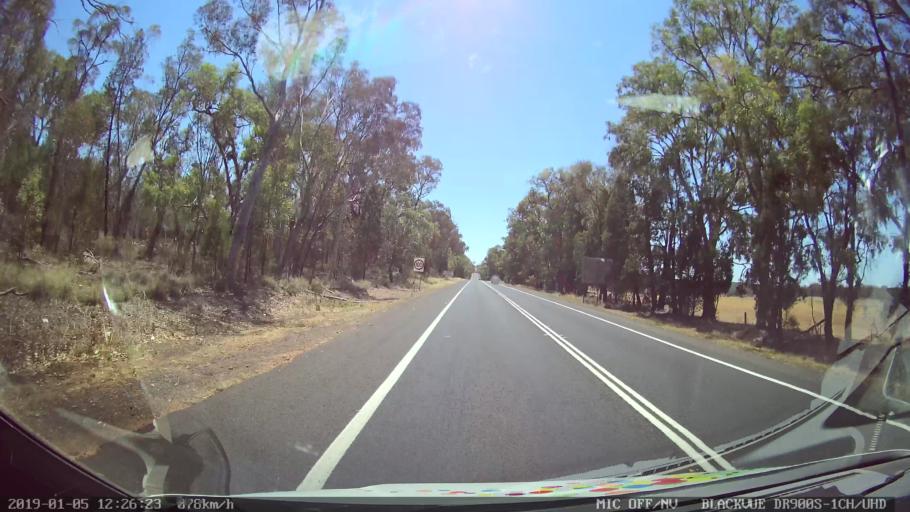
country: AU
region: New South Wales
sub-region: Warrumbungle Shire
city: Coonabarabran
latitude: -31.2547
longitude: 149.2952
